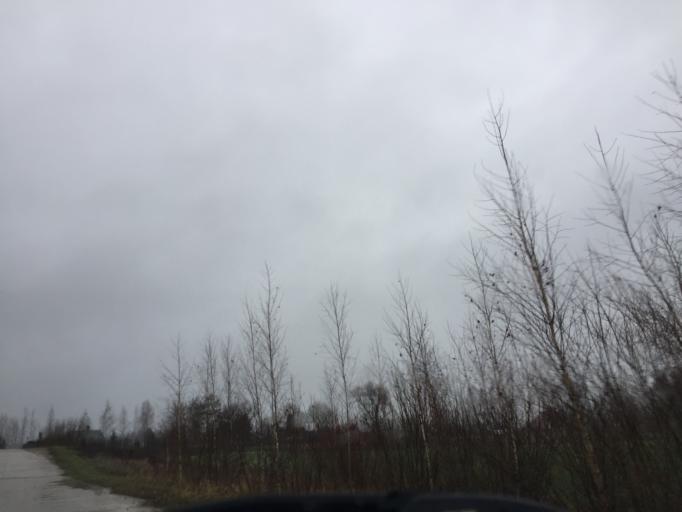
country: LV
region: Jekabpils Rajons
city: Jekabpils
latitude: 56.5116
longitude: 25.8265
